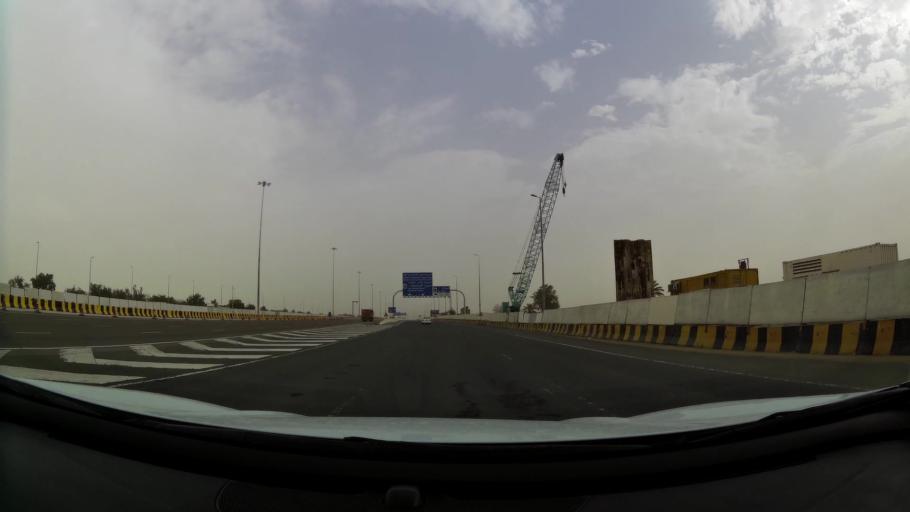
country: AE
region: Abu Dhabi
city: Abu Dhabi
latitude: 24.4741
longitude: 54.6360
